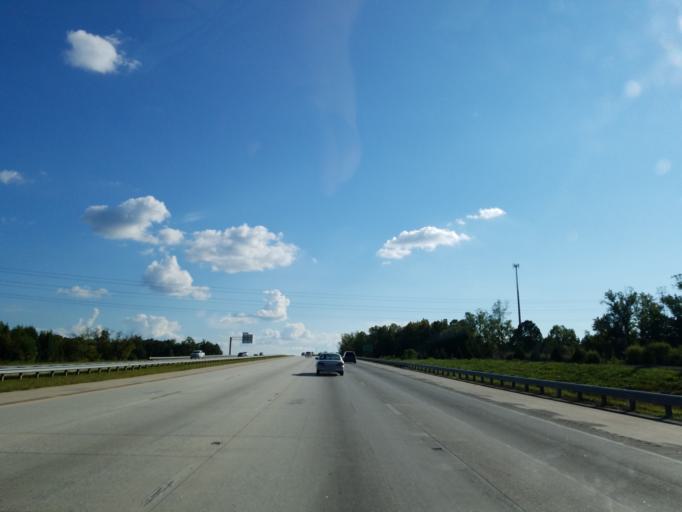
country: US
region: North Carolina
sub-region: Rowan County
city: Spencer
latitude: 35.7118
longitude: -80.3949
